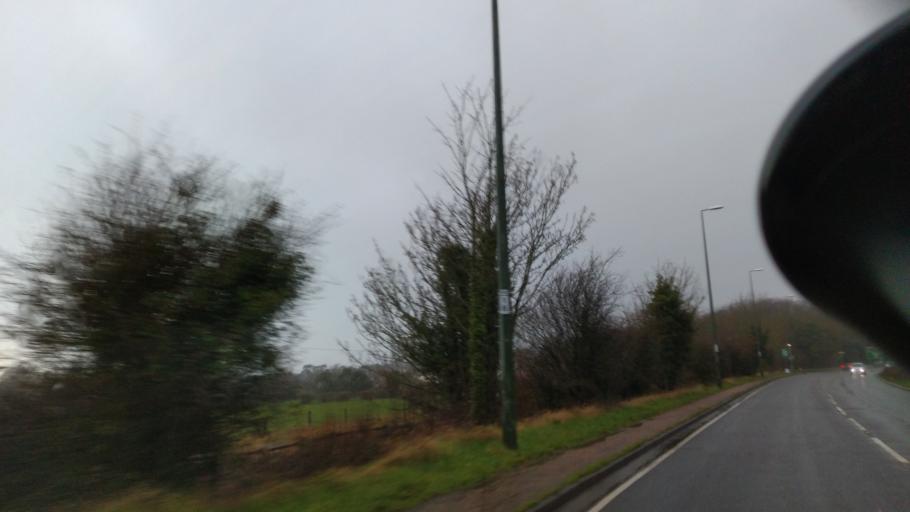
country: GB
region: England
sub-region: West Sussex
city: Arundel
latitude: 50.8501
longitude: -0.5562
